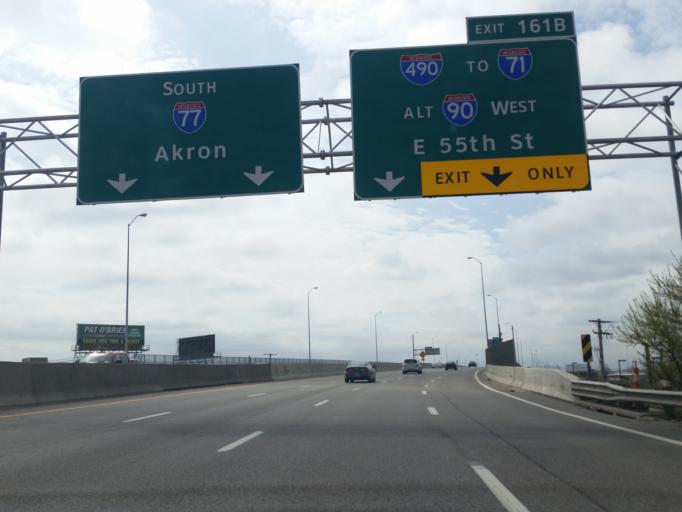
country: US
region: Ohio
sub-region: Cuyahoga County
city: Cleveland
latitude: 41.4883
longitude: -81.6649
